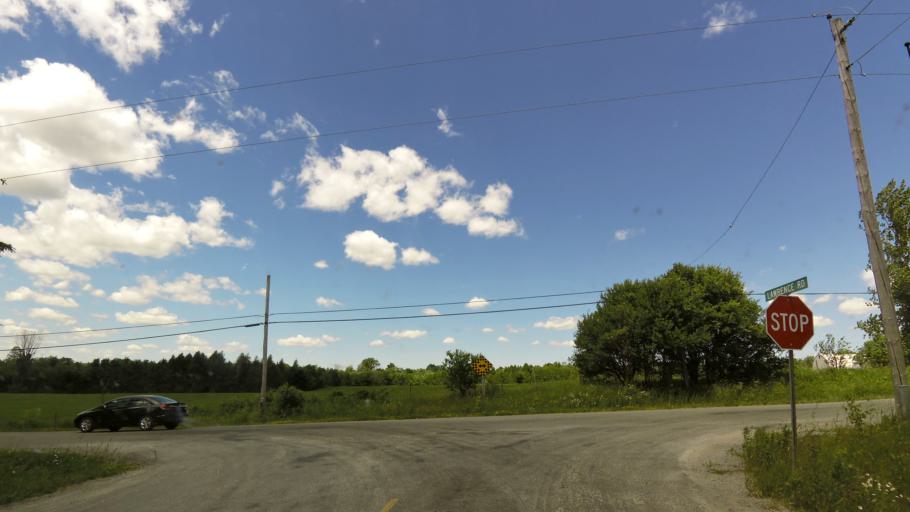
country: CA
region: Ontario
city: Oshawa
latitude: 43.9762
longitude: -78.5901
